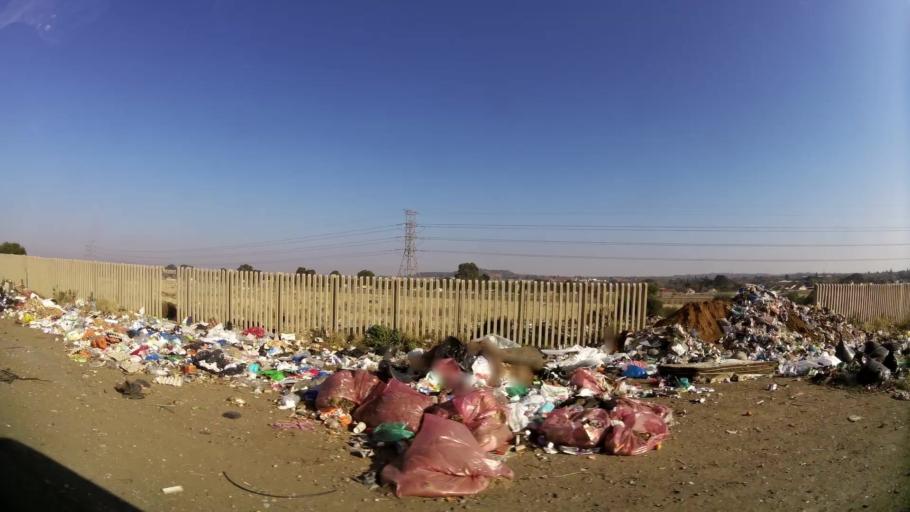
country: ZA
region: Orange Free State
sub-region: Mangaung Metropolitan Municipality
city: Bloemfontein
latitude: -29.1743
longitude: 26.1959
